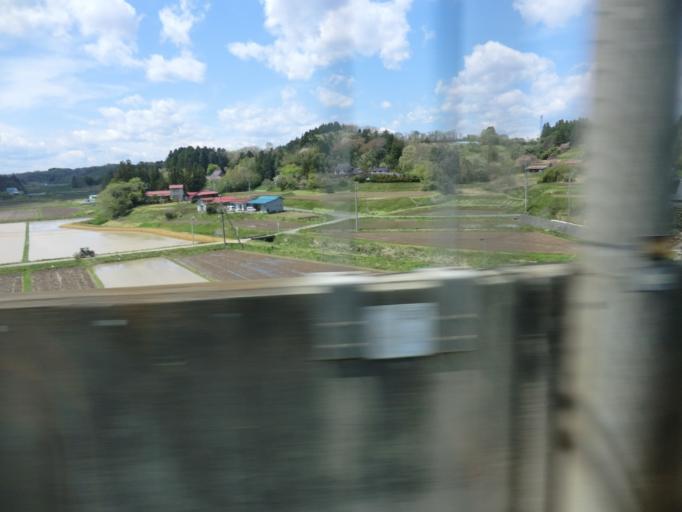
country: JP
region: Miyagi
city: Kogota
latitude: 38.7039
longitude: 141.0458
